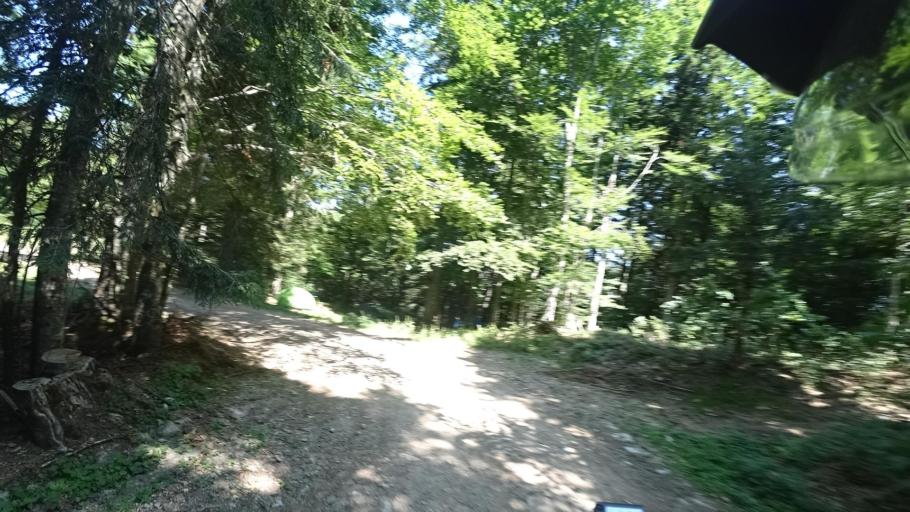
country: HR
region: Licko-Senjska
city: Popovaca
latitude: 44.5936
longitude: 15.1756
